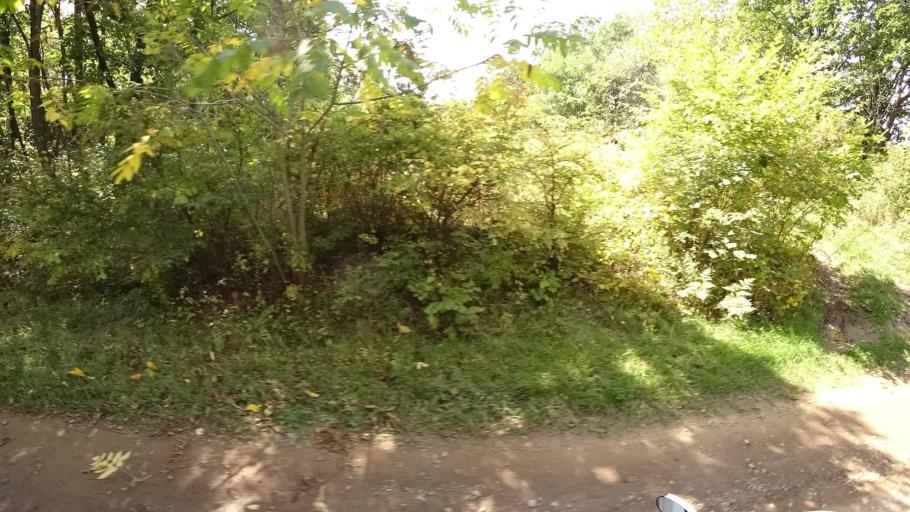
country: RU
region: Primorskiy
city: Kirovskiy
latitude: 44.7605
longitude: 133.6199
